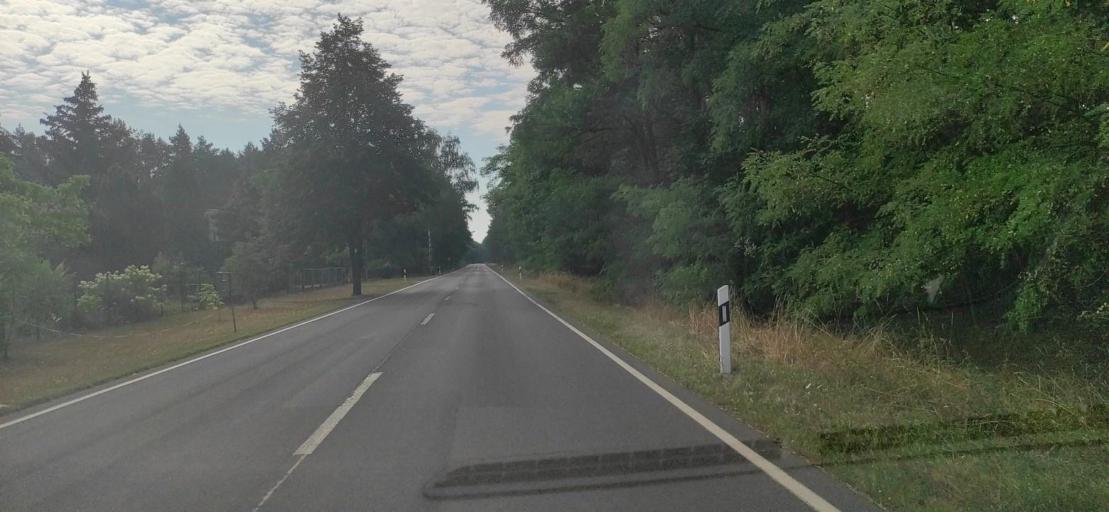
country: DE
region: Brandenburg
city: Forst
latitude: 51.7130
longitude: 14.6697
